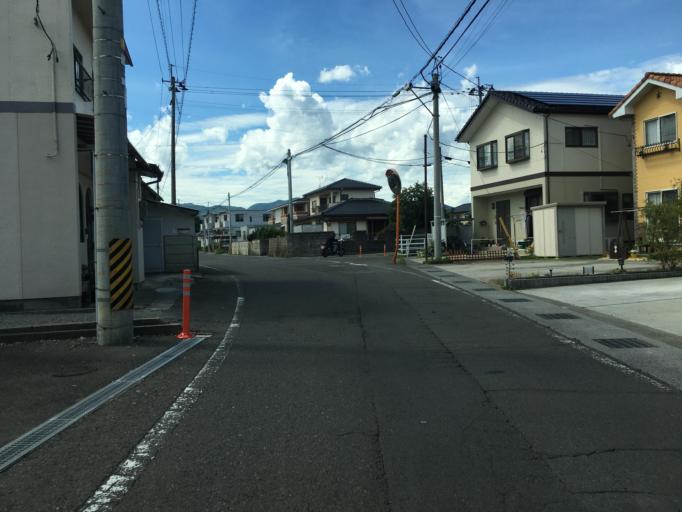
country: JP
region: Fukushima
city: Fukushima-shi
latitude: 37.7736
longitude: 140.4217
